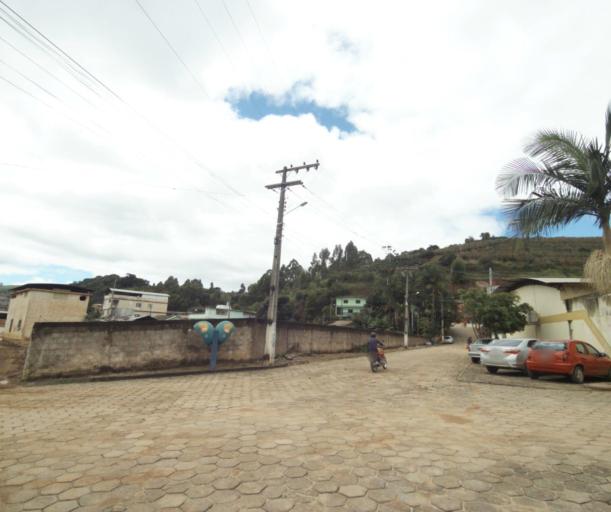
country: BR
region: Espirito Santo
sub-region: Irupi
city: Irupi
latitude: -20.3482
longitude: -41.6466
